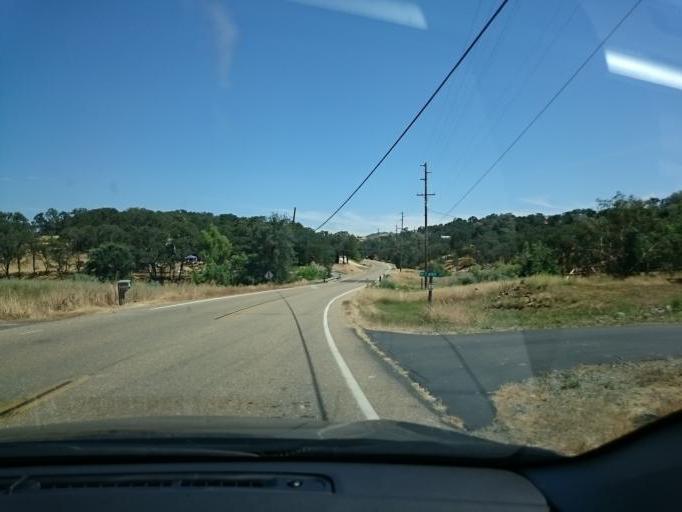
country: US
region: California
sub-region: Calaveras County
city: Rancho Calaveras
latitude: 38.1570
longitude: -120.8390
